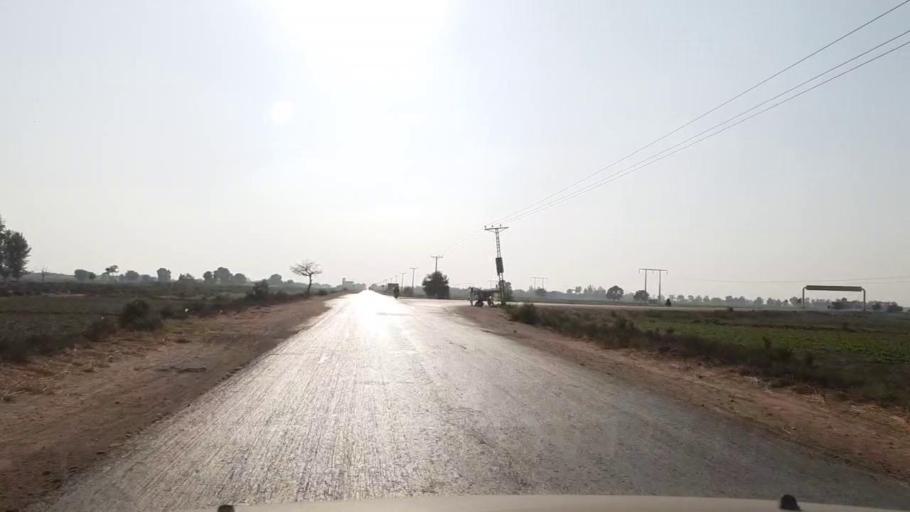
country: PK
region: Sindh
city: Bulri
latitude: 25.0141
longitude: 68.4060
